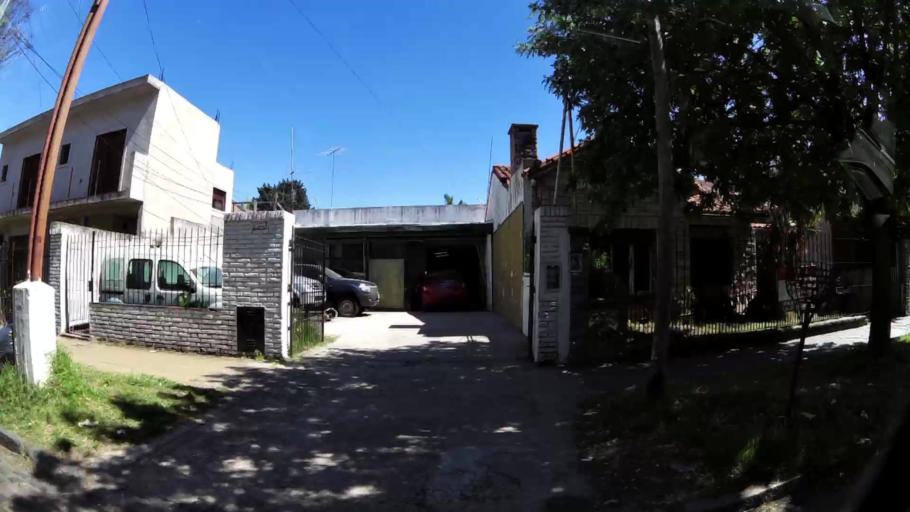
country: AR
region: Buenos Aires
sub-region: Partido de Vicente Lopez
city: Olivos
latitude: -34.5208
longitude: -58.5052
